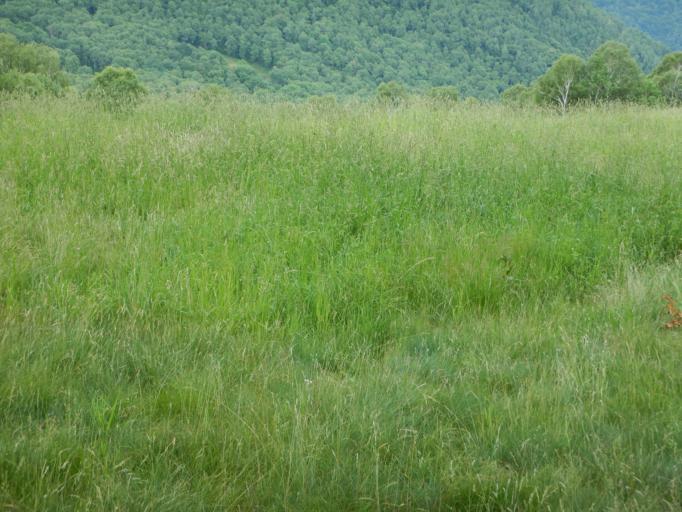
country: CH
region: Ticino
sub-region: Bellinzona District
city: Cadenazzo
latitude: 46.1285
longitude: 8.9584
